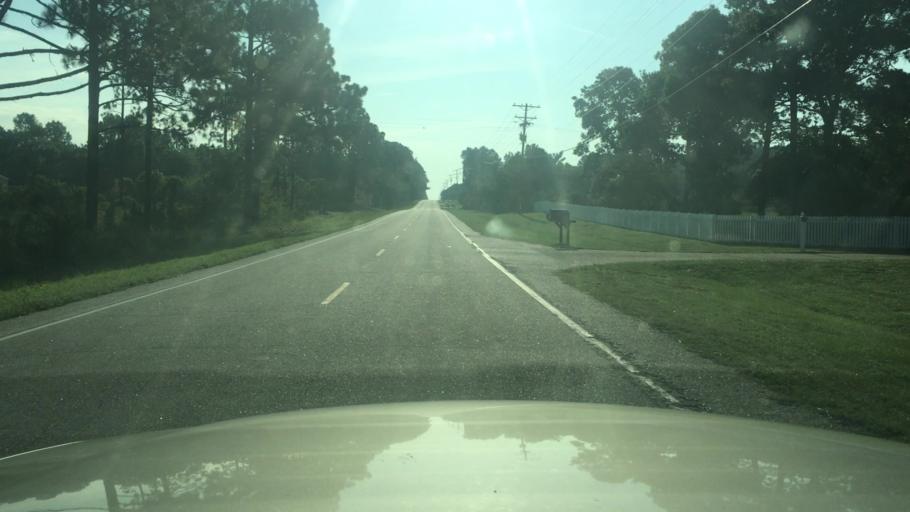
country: US
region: North Carolina
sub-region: Harnett County
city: Walkertown
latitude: 35.2070
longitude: -78.8770
